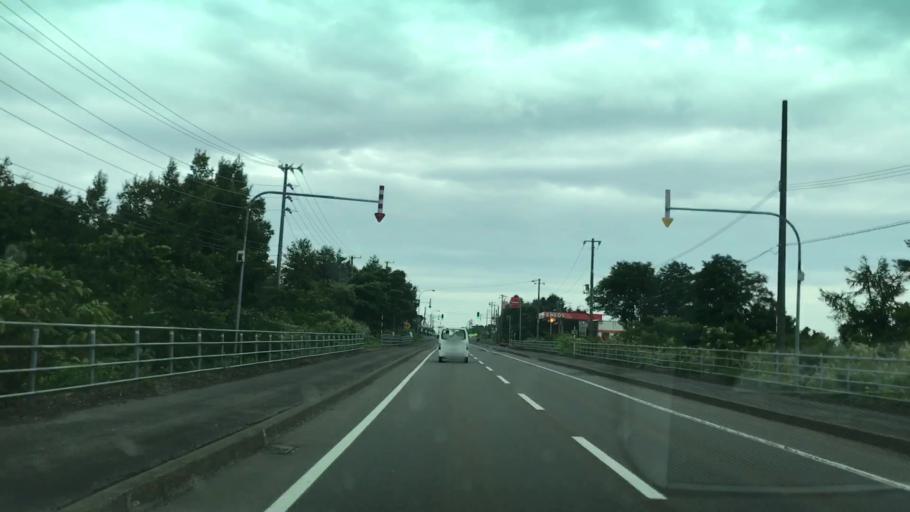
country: JP
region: Hokkaido
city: Iwanai
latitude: 42.7846
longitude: 140.2357
